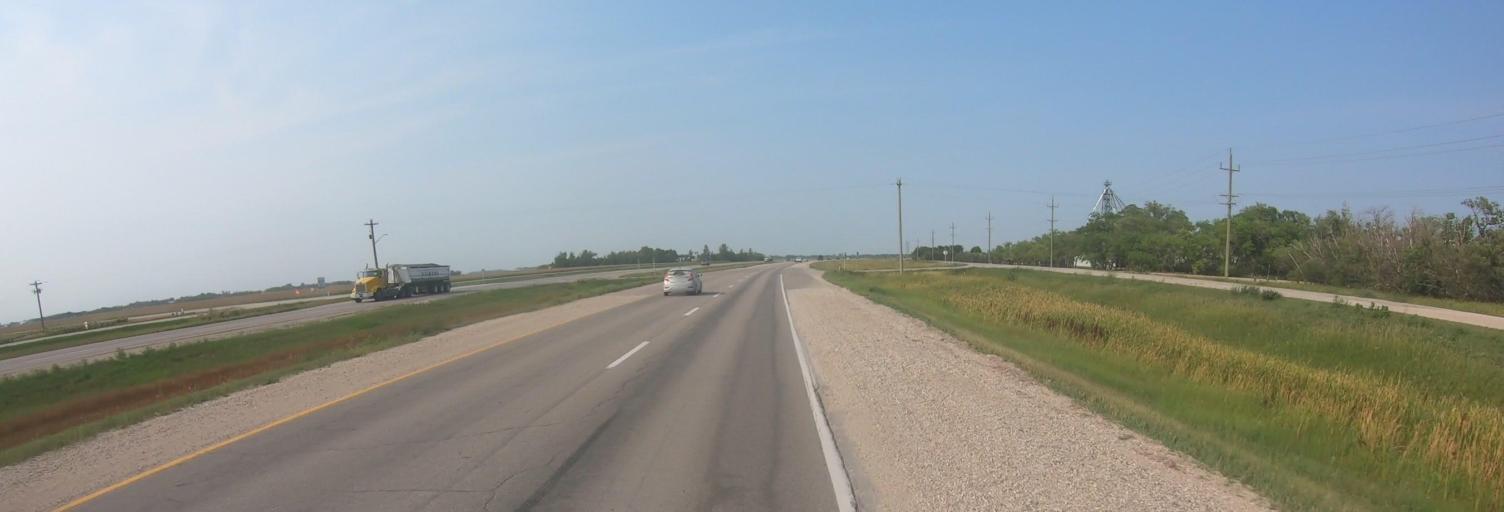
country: CA
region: Manitoba
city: Steinbach
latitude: 49.6331
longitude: -96.6868
